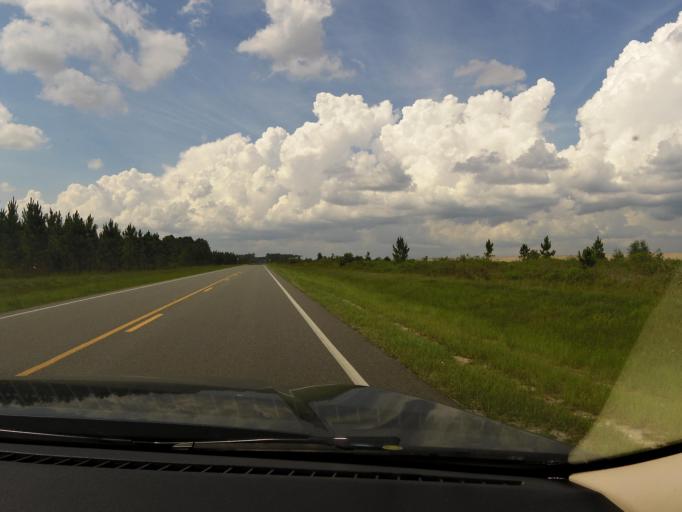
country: US
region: Florida
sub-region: Baker County
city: Macclenny
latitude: 30.2269
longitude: -82.0763
